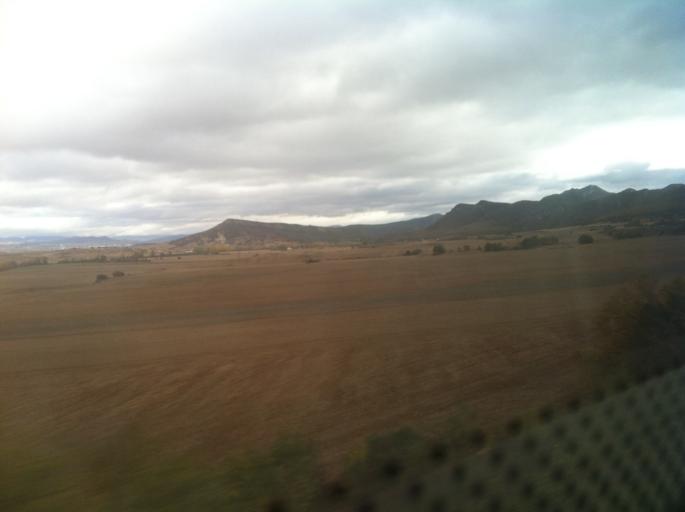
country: ES
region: Castille and Leon
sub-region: Provincia de Burgos
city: Ameyugo
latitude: 42.6517
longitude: -3.0537
